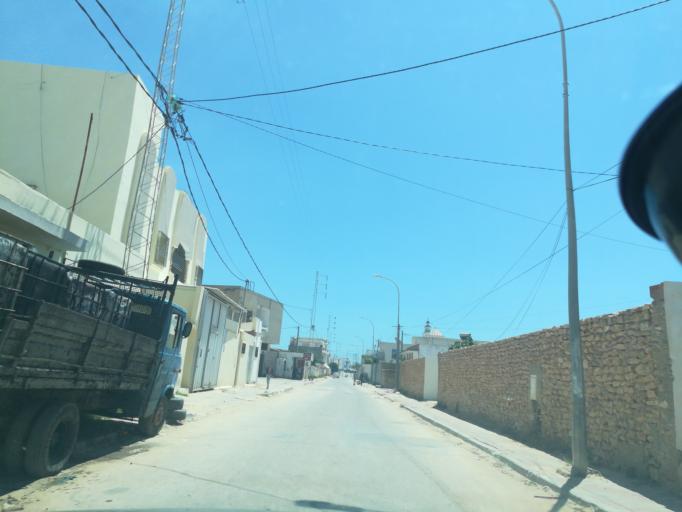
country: TN
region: Safaqis
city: Al Qarmadah
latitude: 34.8206
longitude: 10.7574
